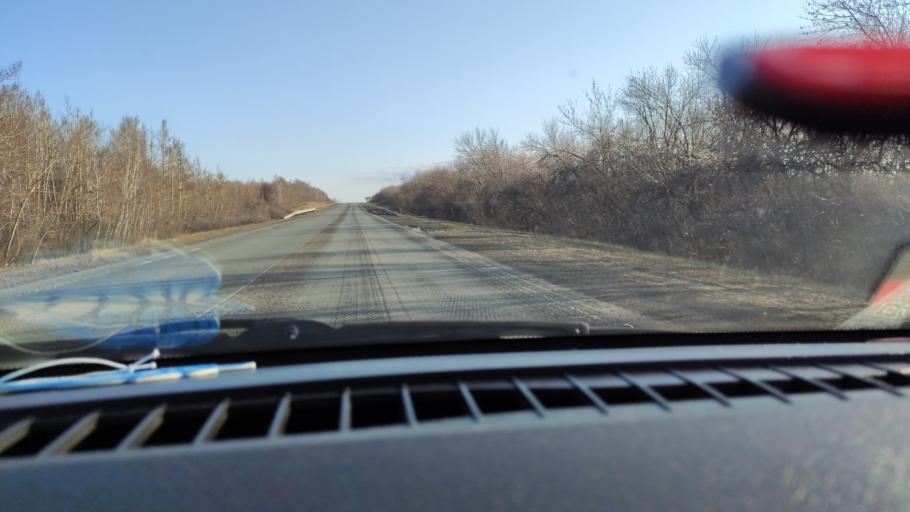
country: RU
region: Saratov
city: Dukhovnitskoye
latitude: 52.6322
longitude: 48.1850
